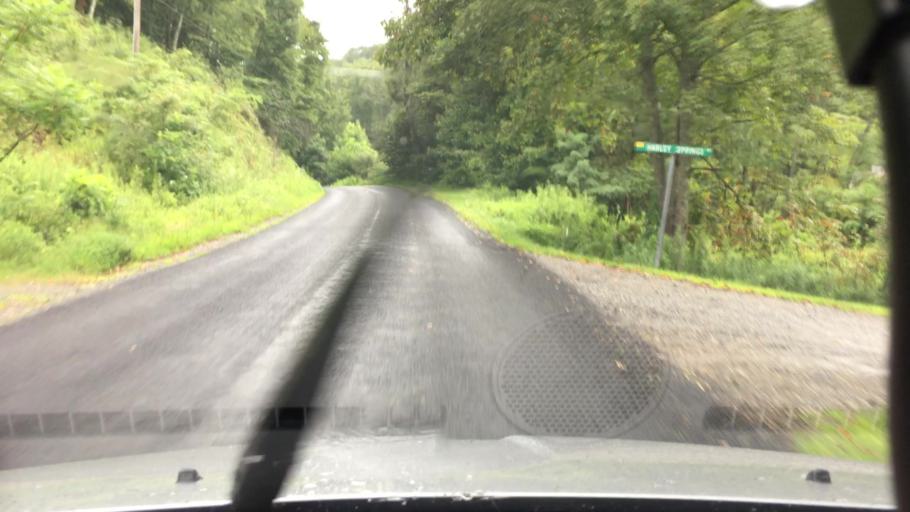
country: US
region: North Carolina
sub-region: Madison County
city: Mars Hill
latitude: 35.9133
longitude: -82.4955
